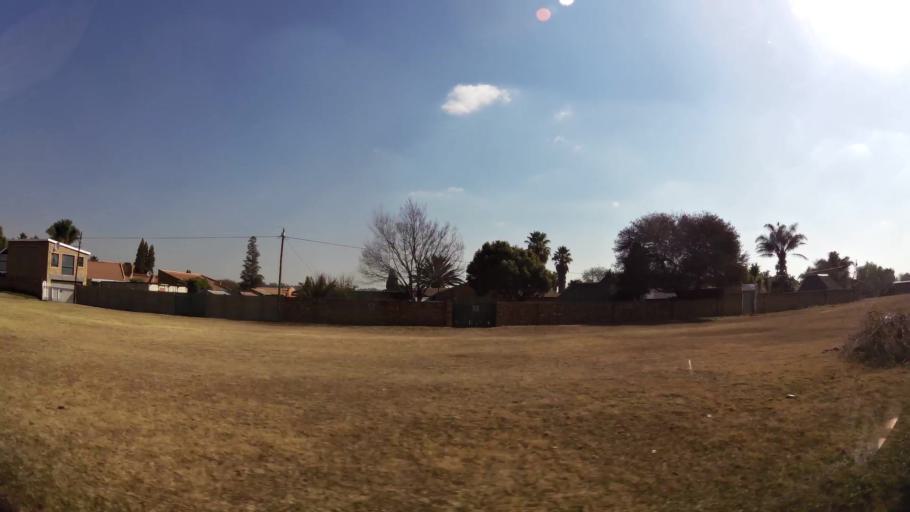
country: ZA
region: Gauteng
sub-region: West Rand District Municipality
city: Randfontein
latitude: -26.1520
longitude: 27.6910
